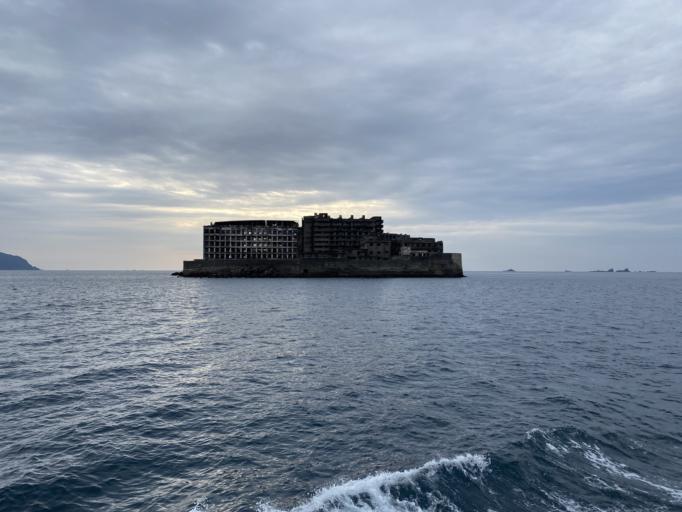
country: JP
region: Nagasaki
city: Nagasaki-shi
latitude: 32.6313
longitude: 129.7410
